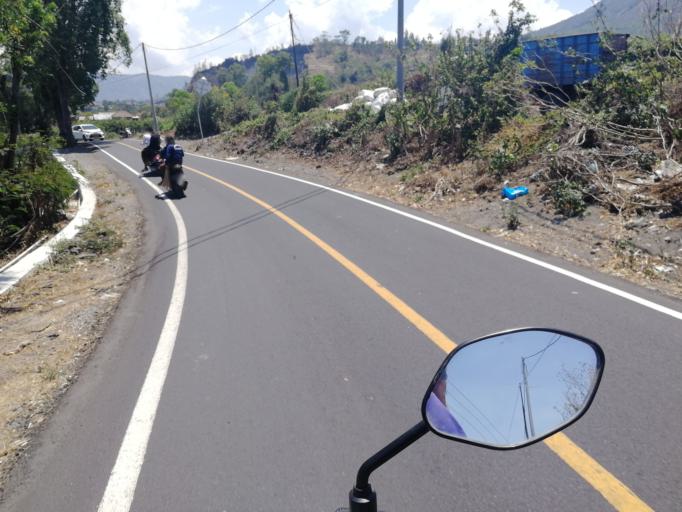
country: ID
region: Bali
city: Banjar Trunyan
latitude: -8.2322
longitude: 115.4058
